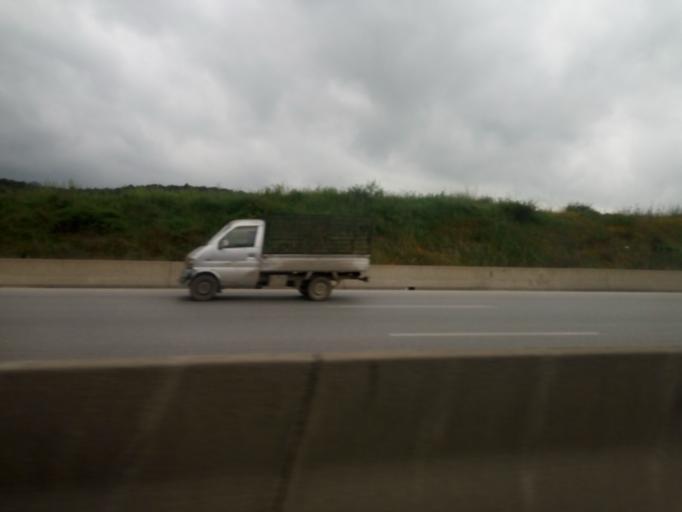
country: DZ
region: Bouira
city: Lakhdaria
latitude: 36.5782
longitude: 3.5499
